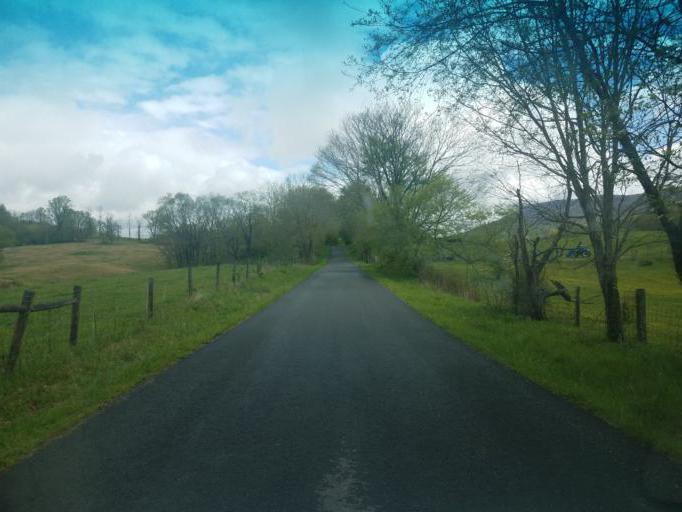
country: US
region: Virginia
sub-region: Smyth County
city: Atkins
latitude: 36.9515
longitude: -81.4095
